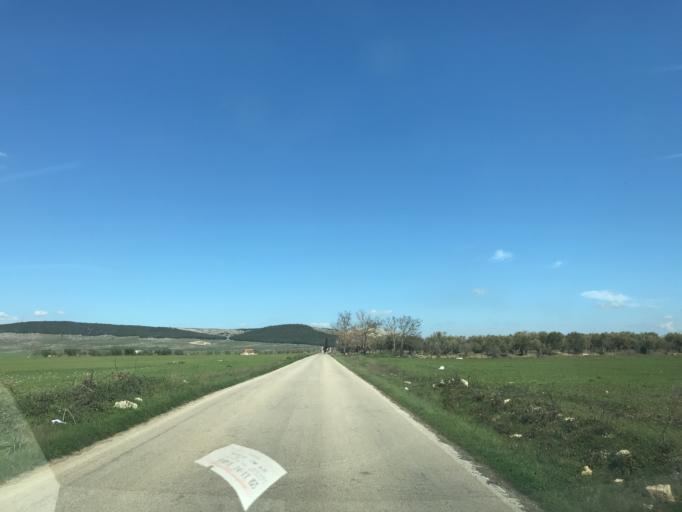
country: IT
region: Apulia
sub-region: Provincia di Bari
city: Gravina in Puglia
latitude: 40.8522
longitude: 16.4303
